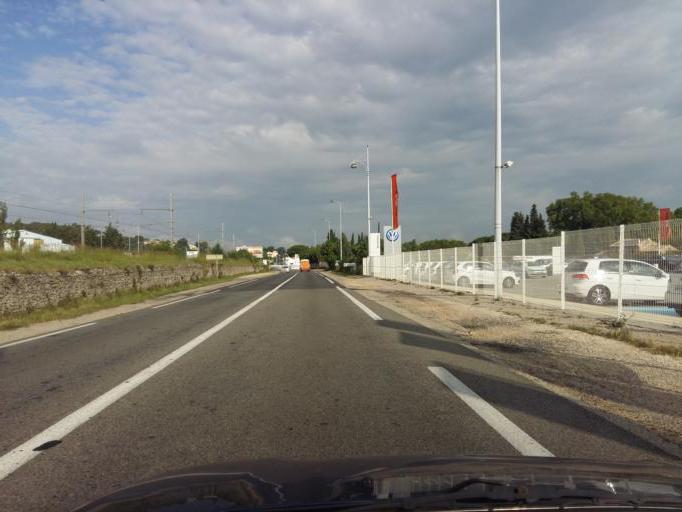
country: FR
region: Languedoc-Roussillon
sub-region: Departement du Gard
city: Bagnols-sur-Ceze
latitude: 44.1545
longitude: 4.6428
